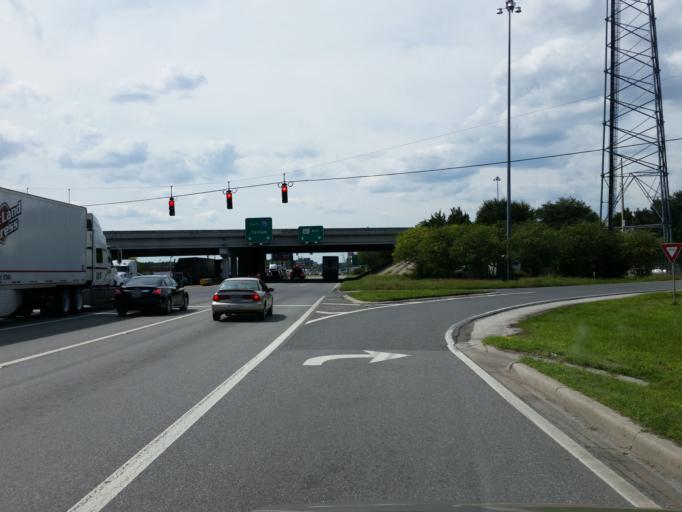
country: US
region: Florida
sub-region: Sumter County
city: Wildwood
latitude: 28.8734
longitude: -82.0912
